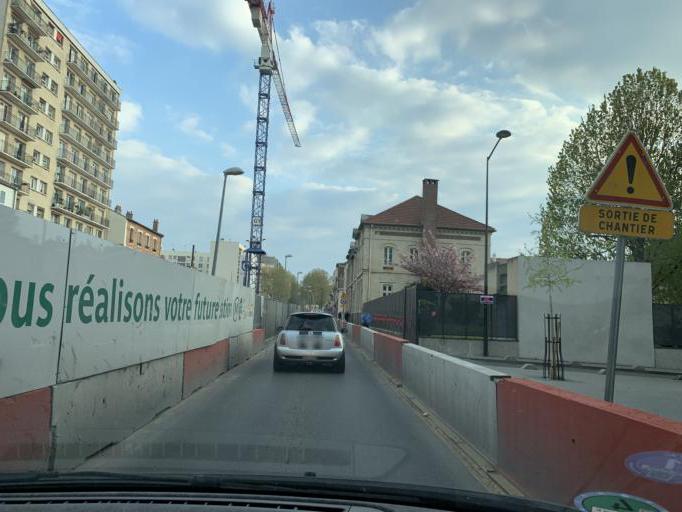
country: FR
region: Ile-de-France
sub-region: Departement de Seine-Saint-Denis
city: Aubervilliers
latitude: 48.9133
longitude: 2.3804
